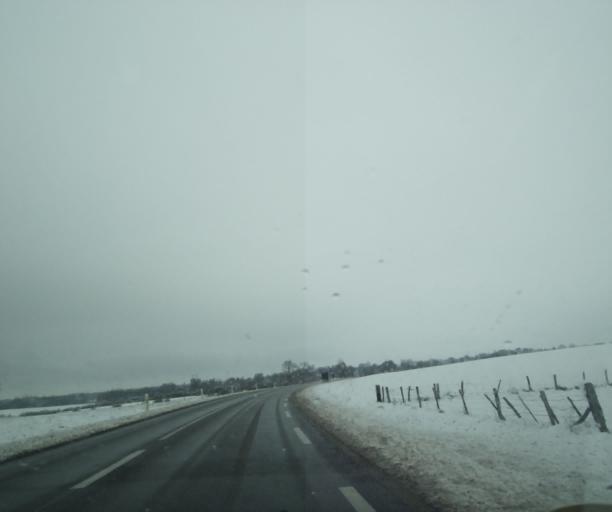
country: FR
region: Champagne-Ardenne
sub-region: Departement de la Haute-Marne
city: Montier-en-Der
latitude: 48.5117
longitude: 4.8029
